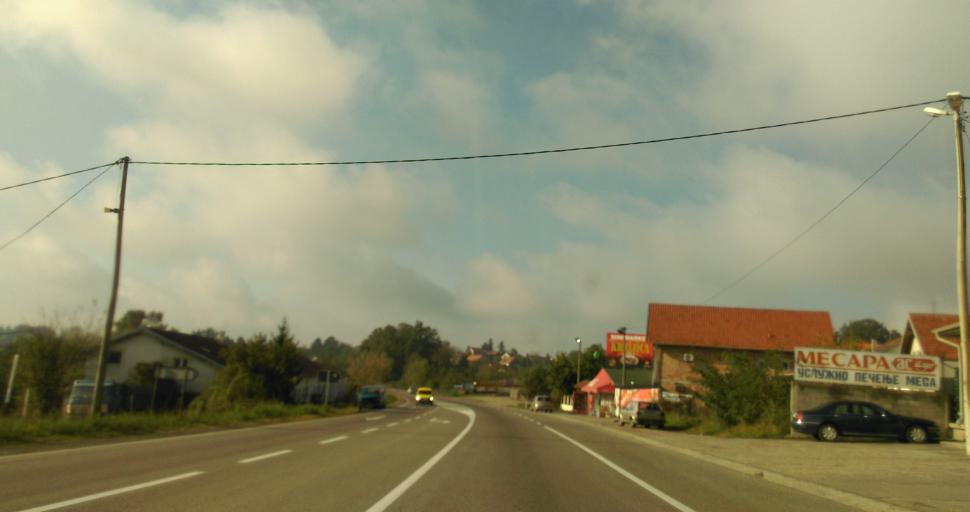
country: RS
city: Vranic
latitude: 44.6069
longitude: 20.3558
